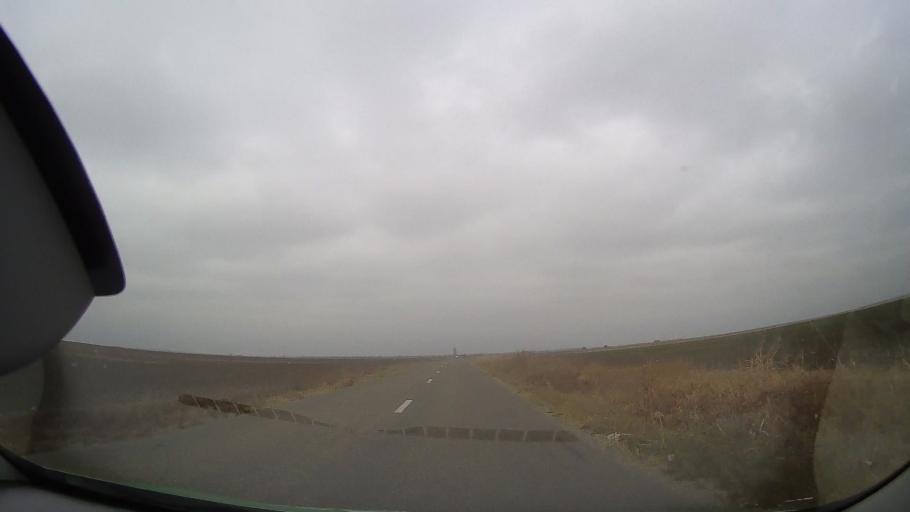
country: RO
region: Buzau
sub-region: Comuna Bradeanu
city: Bradeanu
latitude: 44.8950
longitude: 26.8734
